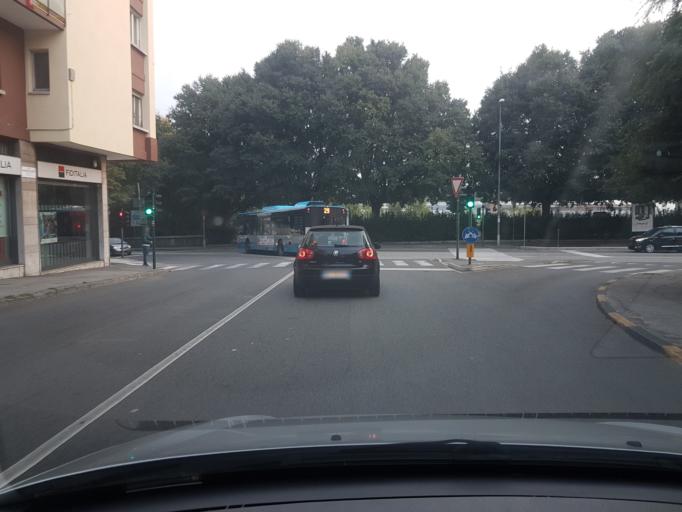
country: IT
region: Friuli Venezia Giulia
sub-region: Provincia di Trieste
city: Trieste
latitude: 45.6401
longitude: 13.7750
